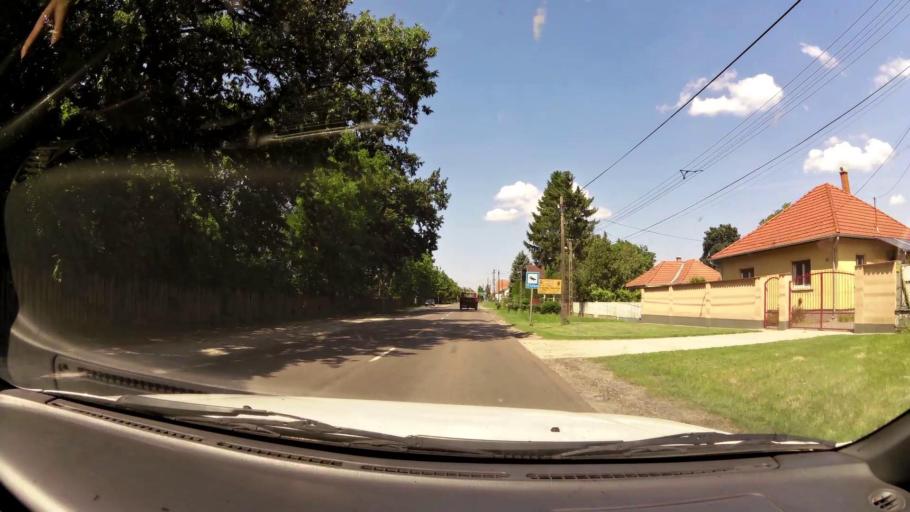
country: HU
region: Pest
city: Tapioszolos
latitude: 47.2509
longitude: 19.8487
